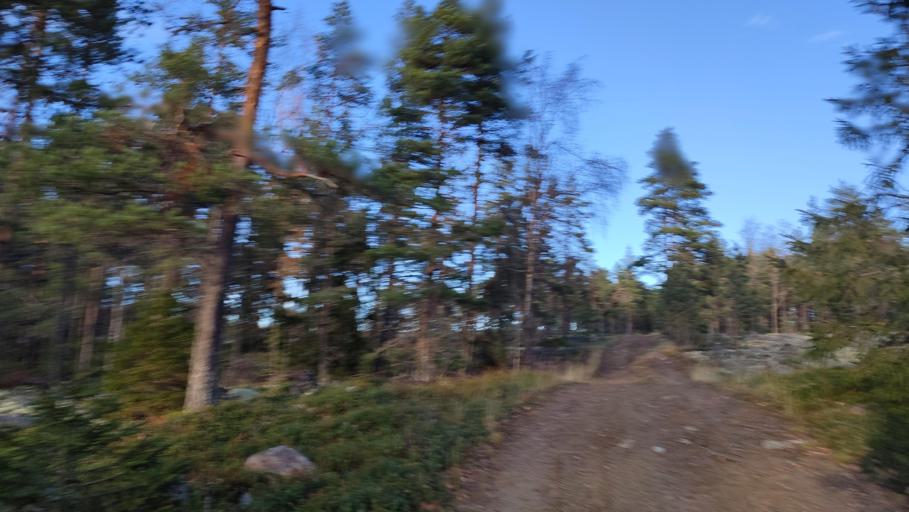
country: FI
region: Southern Ostrobothnia
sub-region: Suupohja
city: Karijoki
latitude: 62.2826
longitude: 21.6438
